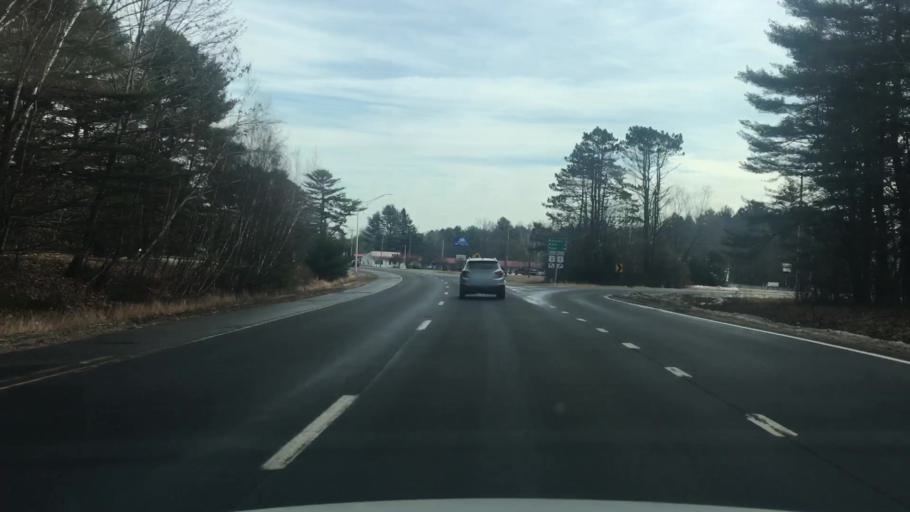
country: US
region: Maine
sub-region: Sagadahoc County
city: Topsham
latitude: 43.9127
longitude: -70.0026
